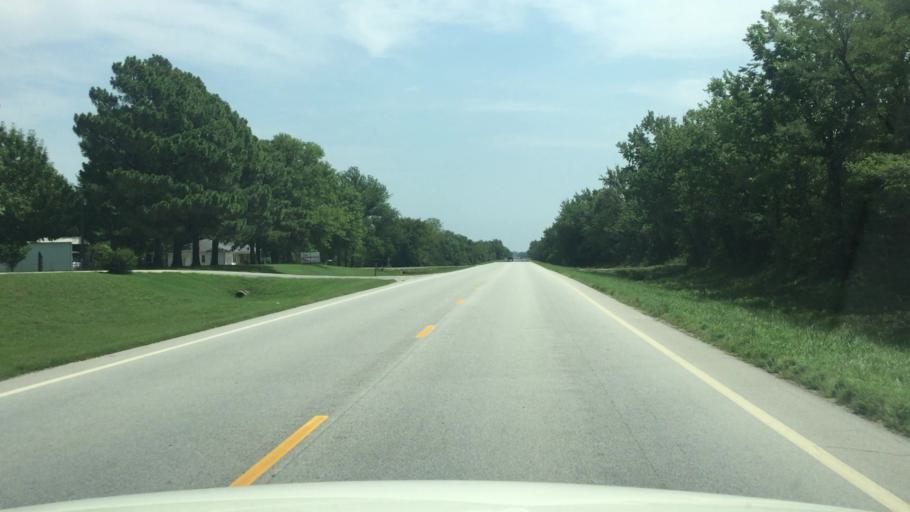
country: US
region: Kansas
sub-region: Cherokee County
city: Columbus
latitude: 37.1788
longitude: -94.8790
